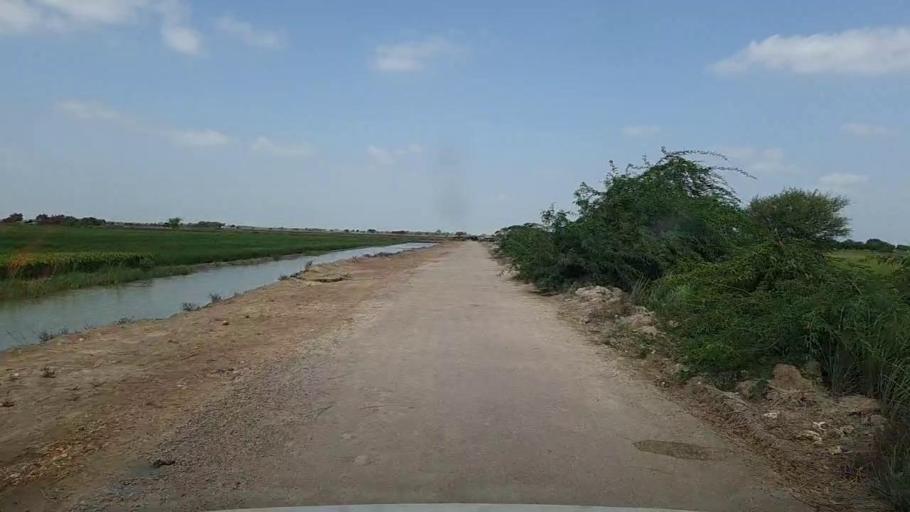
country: PK
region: Sindh
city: Kario
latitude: 24.6794
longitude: 68.5879
